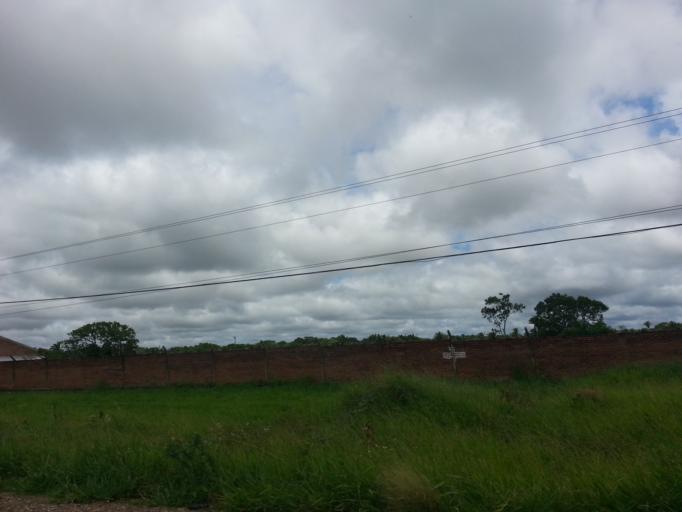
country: BO
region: Santa Cruz
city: La Belgica
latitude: -17.6499
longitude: -63.1577
